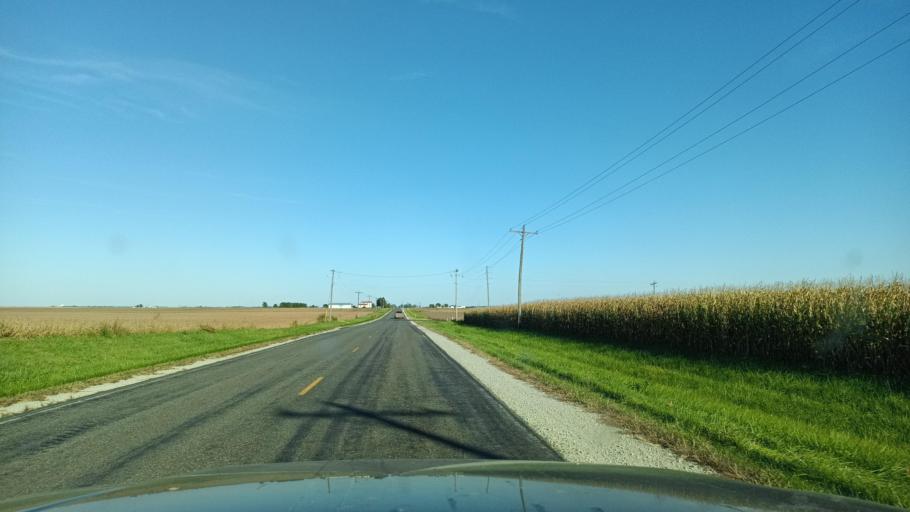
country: US
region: Illinois
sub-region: De Witt County
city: Farmer City
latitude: 40.2241
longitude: -88.7655
